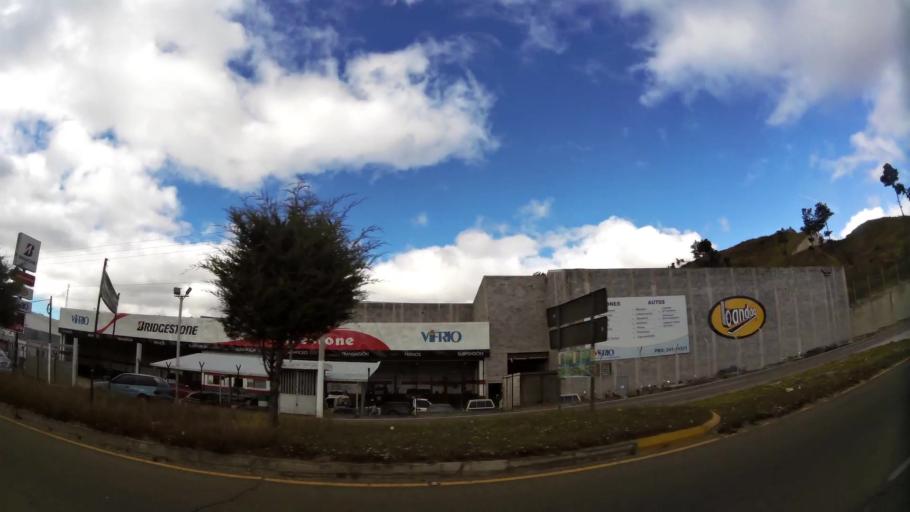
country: GT
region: Quetzaltenango
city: Salcaja
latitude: 14.8698
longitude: -91.4682
